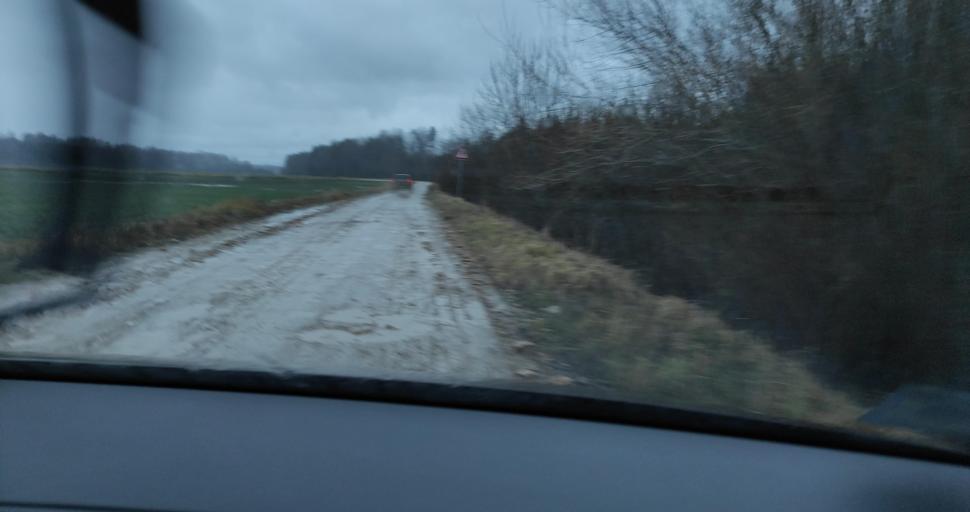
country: LV
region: Skrunda
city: Skrunda
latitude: 56.6249
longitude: 22.2334
